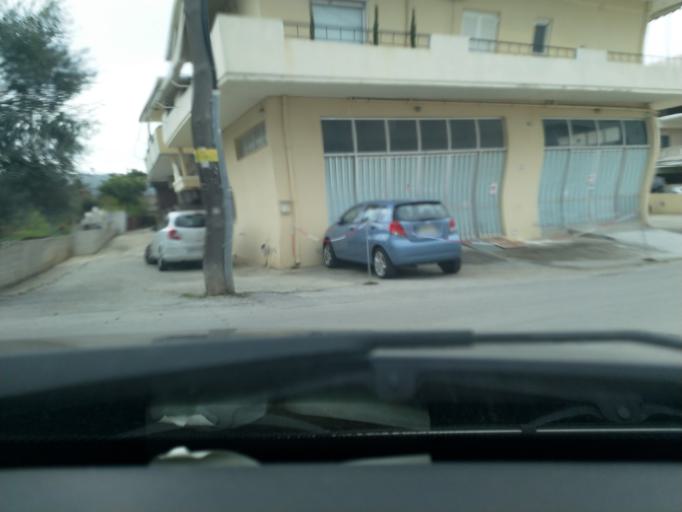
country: GR
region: Crete
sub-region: Nomos Chanias
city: Chania
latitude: 35.5010
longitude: 24.0230
